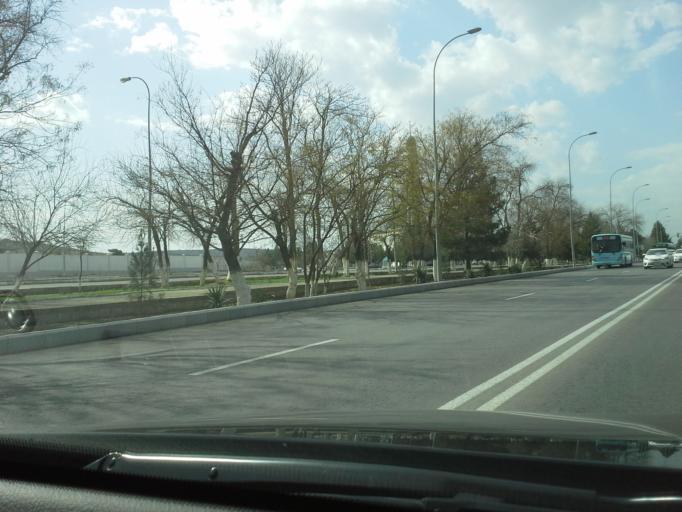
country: TM
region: Ahal
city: Ashgabat
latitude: 37.9555
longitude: 58.3279
